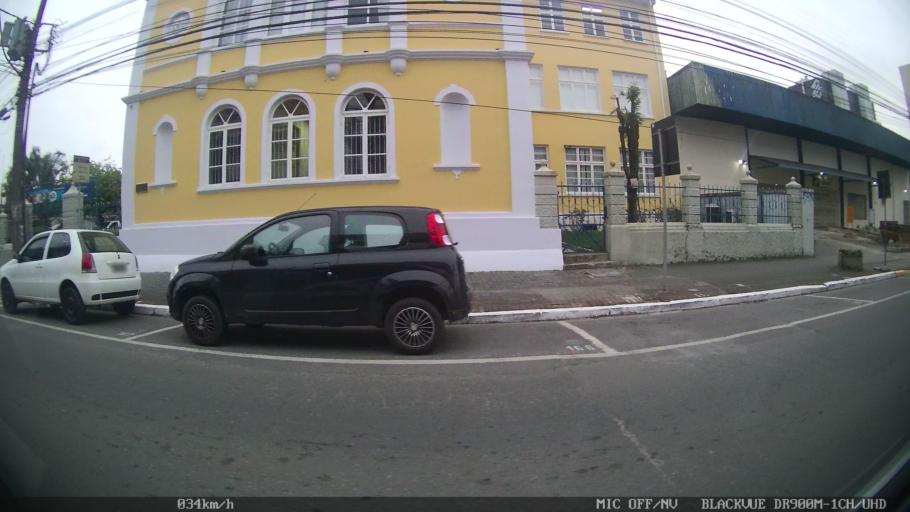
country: BR
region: Santa Catarina
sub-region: Joinville
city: Joinville
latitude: -26.2997
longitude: -48.8465
